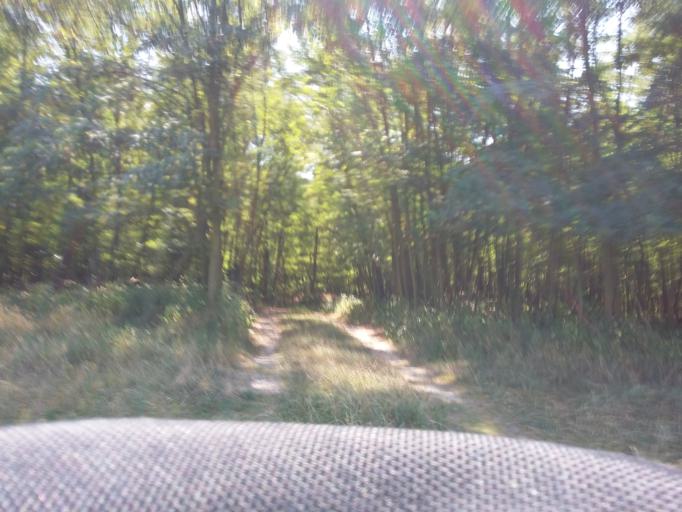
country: SK
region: Bratislavsky
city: Stupava
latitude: 48.3093
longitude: 17.0362
